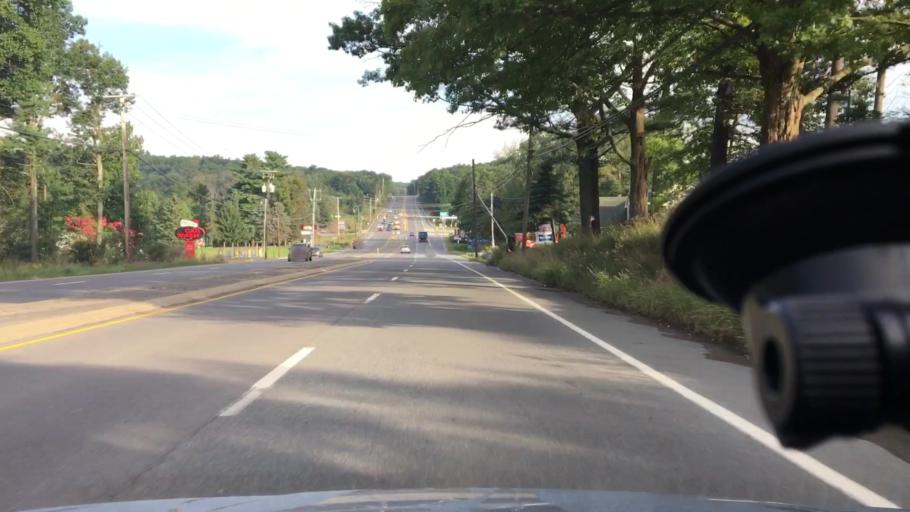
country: US
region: Pennsylvania
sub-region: Monroe County
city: Mount Pocono
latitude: 41.0995
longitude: -75.3335
